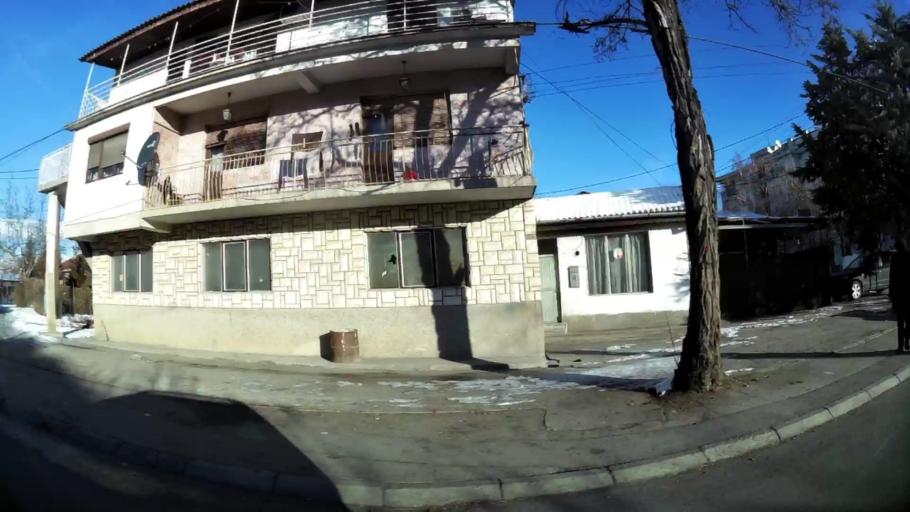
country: MK
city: Krushopek
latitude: 42.0092
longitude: 21.3588
